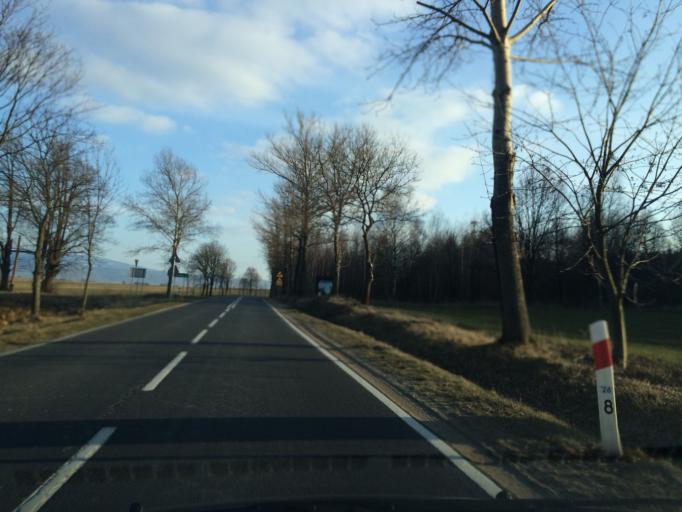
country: PL
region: Lower Silesian Voivodeship
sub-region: Powiat klodzki
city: Bystrzyca Klodzka
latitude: 50.2382
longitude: 16.6745
